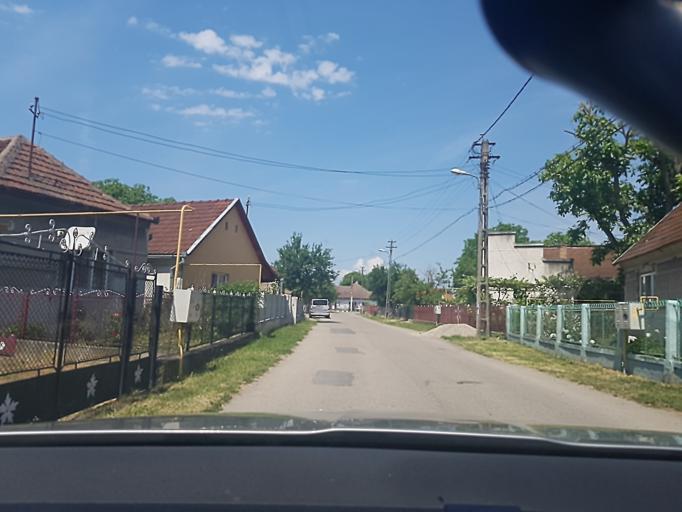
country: RO
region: Hunedoara
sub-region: Comuna Calan
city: Calan
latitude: 45.7401
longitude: 23.0085
